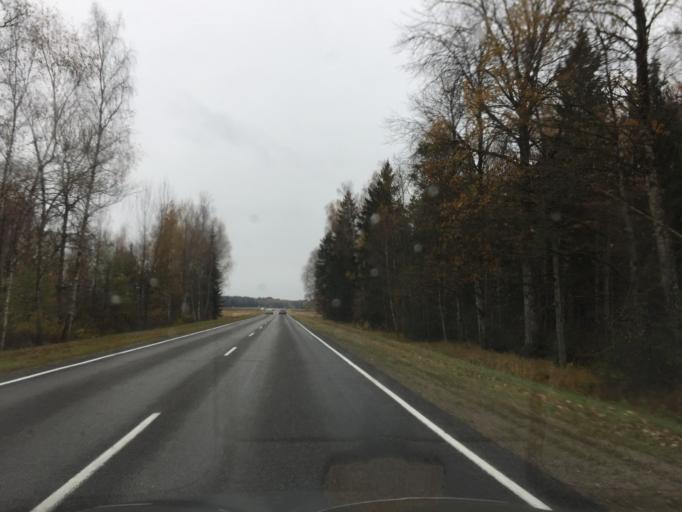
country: BY
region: Mogilev
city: Chavusy
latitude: 53.6869
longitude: 31.1684
